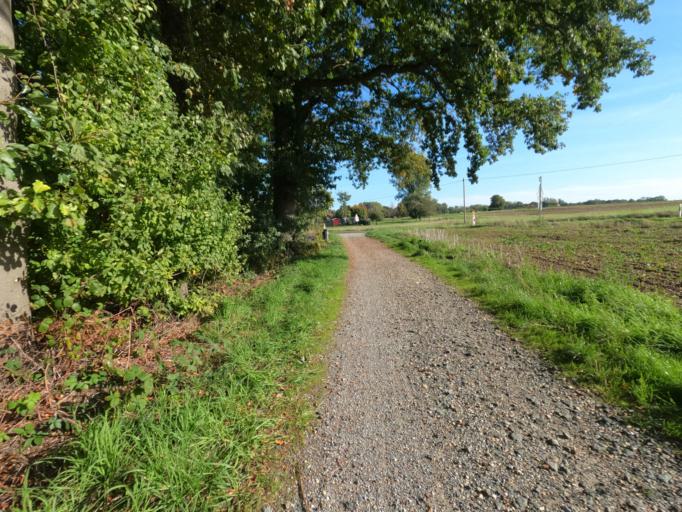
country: DE
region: North Rhine-Westphalia
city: Wegberg
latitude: 51.1767
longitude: 6.2719
